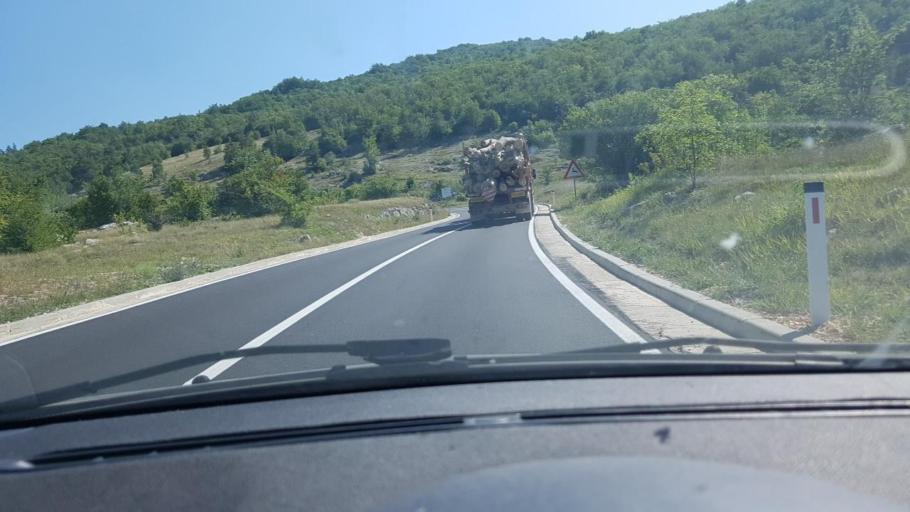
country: BA
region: Federation of Bosnia and Herzegovina
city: Bosansko Grahovo
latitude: 44.2995
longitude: 16.3060
